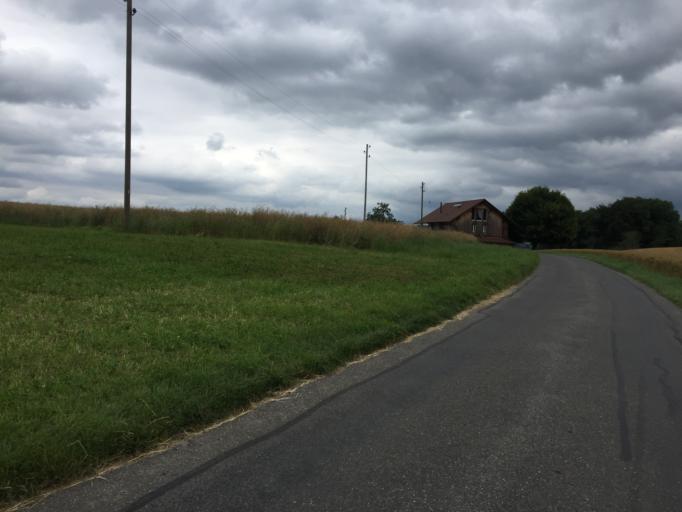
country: CH
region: Bern
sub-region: Bern-Mittelland District
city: Stettlen
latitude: 46.9418
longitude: 7.5297
